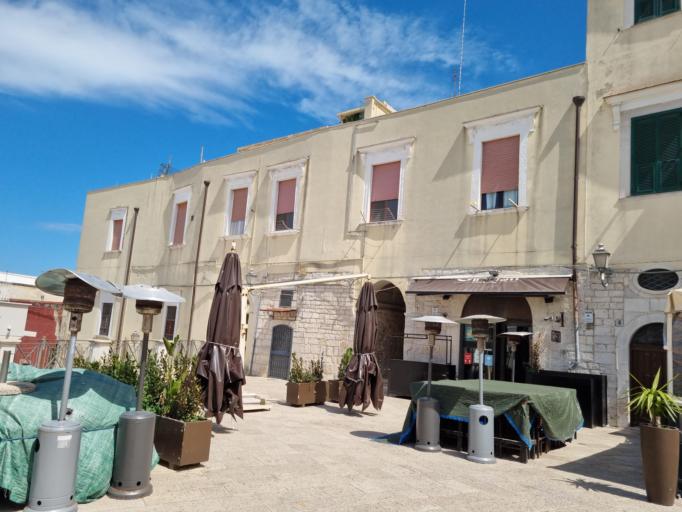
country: IT
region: Apulia
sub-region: Provincia di Barletta - Andria - Trani
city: Barletta
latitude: 41.3214
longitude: 16.2838
